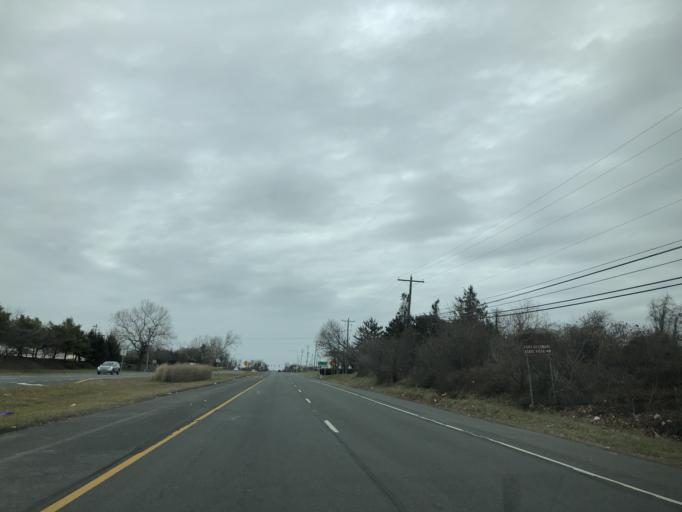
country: US
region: Delaware
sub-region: New Castle County
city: Bear
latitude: 39.5758
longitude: -75.6565
